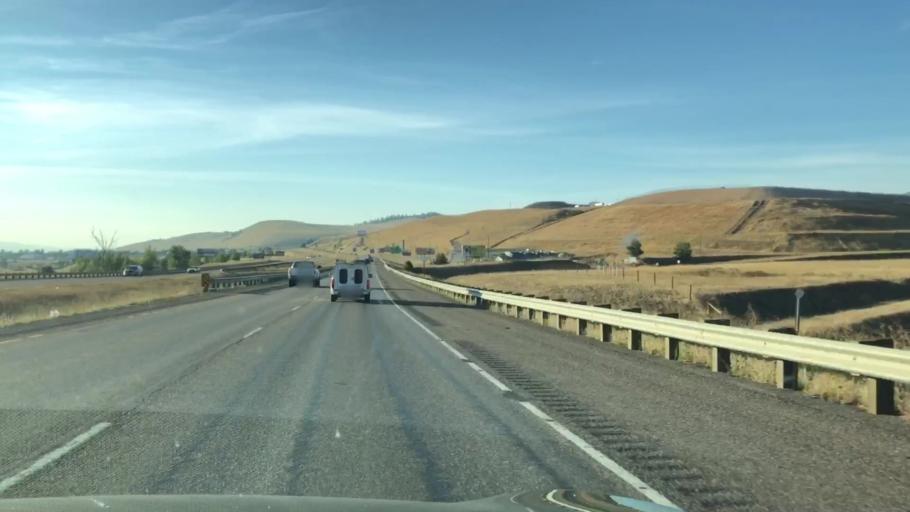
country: US
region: Montana
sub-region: Missoula County
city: Missoula
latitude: 46.8964
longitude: -114.0119
